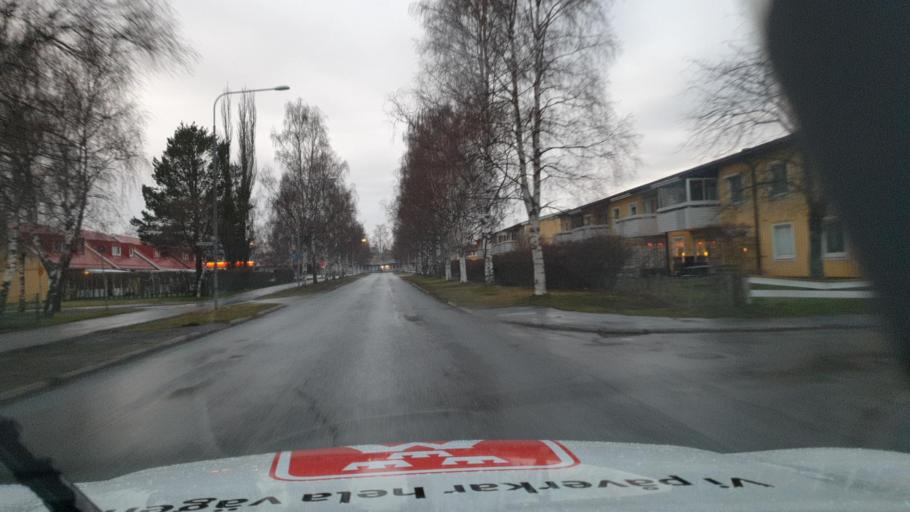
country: SE
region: Vaesterbotten
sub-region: Umea Kommun
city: Roback
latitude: 63.8161
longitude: 20.2139
